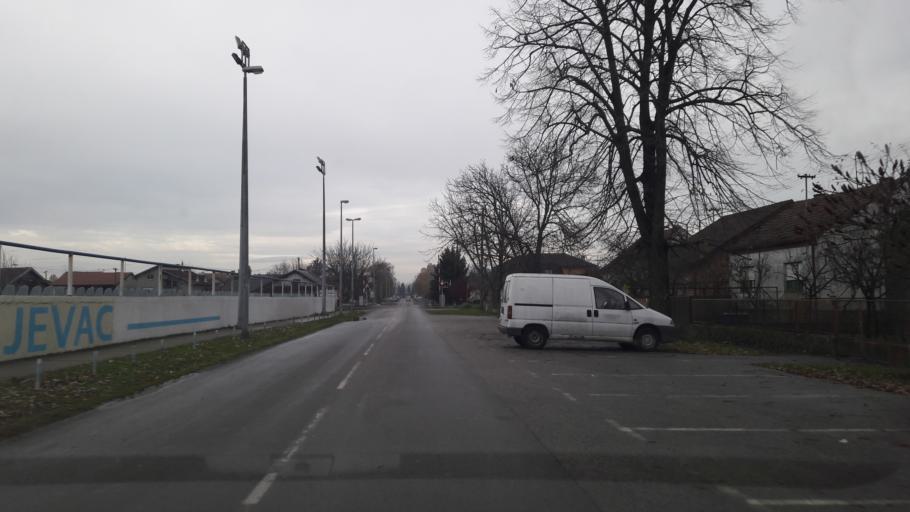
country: HR
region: Osjecko-Baranjska
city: Visnjevac
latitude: 45.5608
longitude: 18.6184
